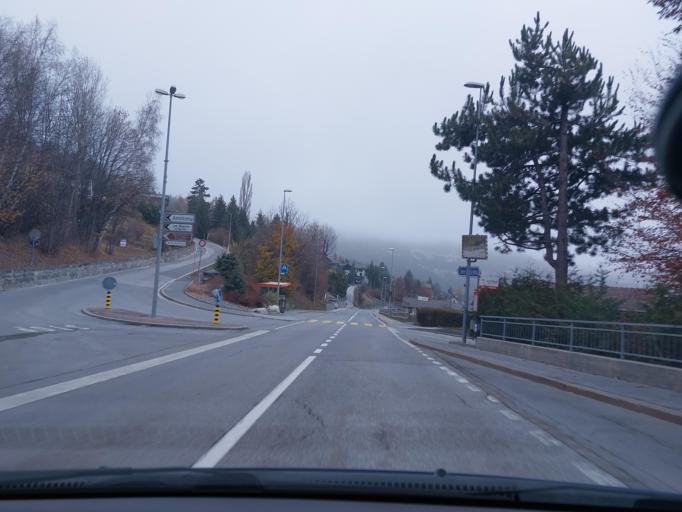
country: CH
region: Valais
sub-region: Sierre District
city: Veyras
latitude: 46.3151
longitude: 7.5184
